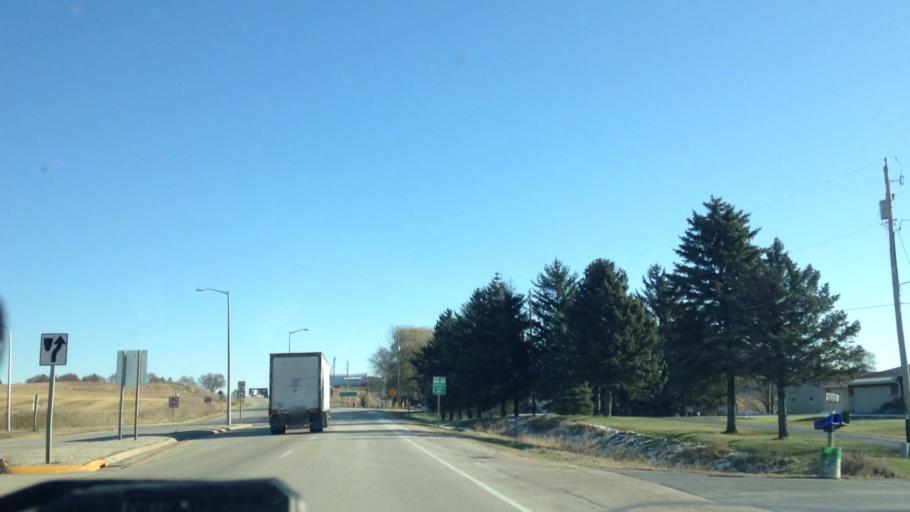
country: US
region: Wisconsin
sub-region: Washington County
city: Slinger
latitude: 43.4244
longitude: -88.3344
